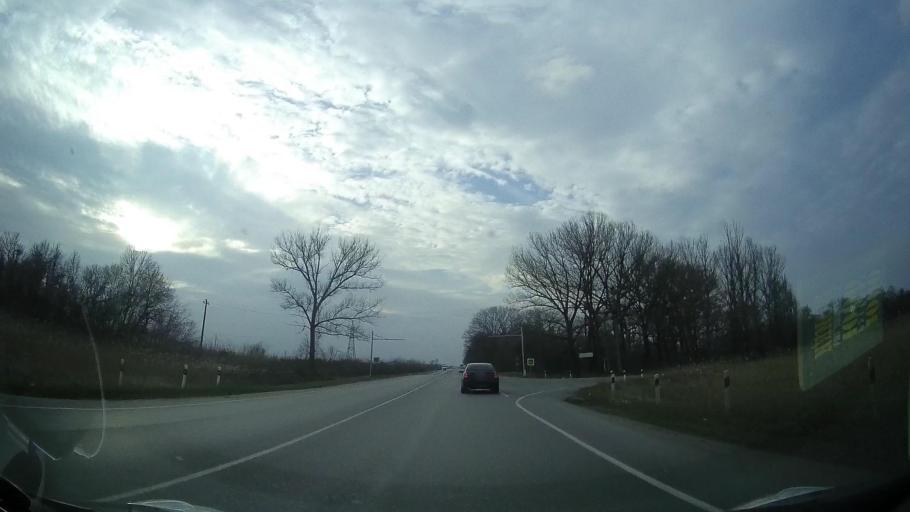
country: RU
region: Rostov
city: Ol'ginskaya
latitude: 47.1315
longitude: 39.9569
